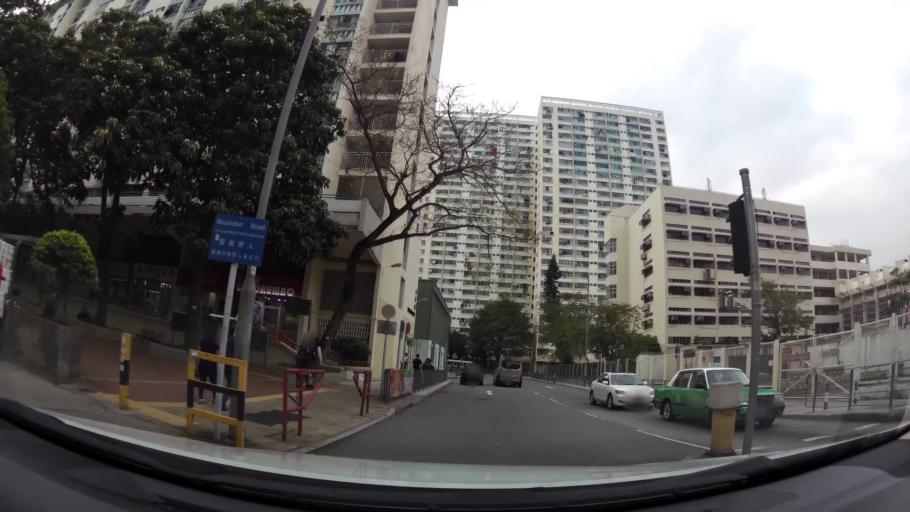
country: HK
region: Tai Po
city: Tai Po
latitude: 22.4543
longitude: 114.1707
